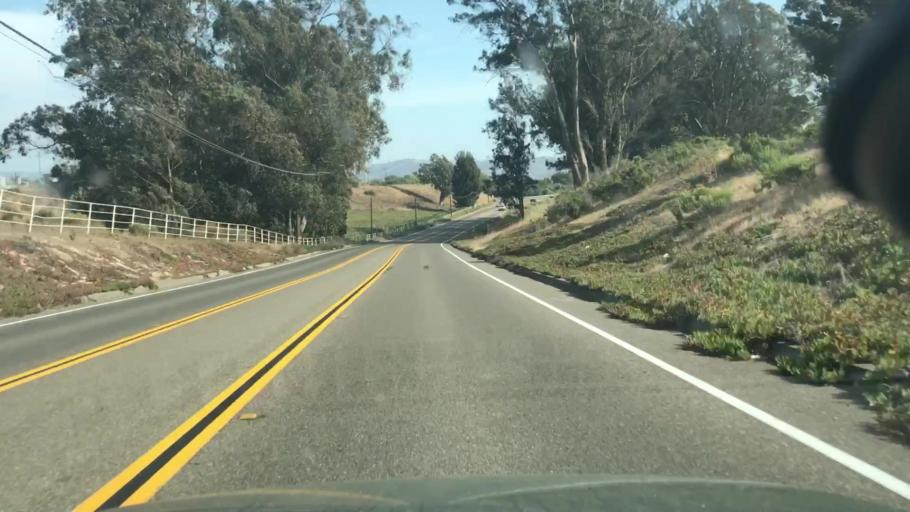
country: US
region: California
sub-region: Santa Barbara County
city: Vandenberg Village
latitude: 34.6766
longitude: -120.4957
